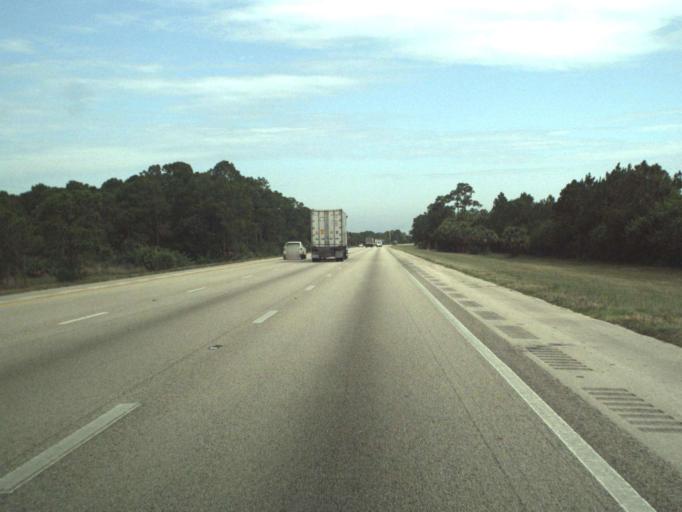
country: US
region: Florida
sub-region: Saint Lucie County
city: Port Saint Lucie
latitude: 27.2326
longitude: -80.4057
